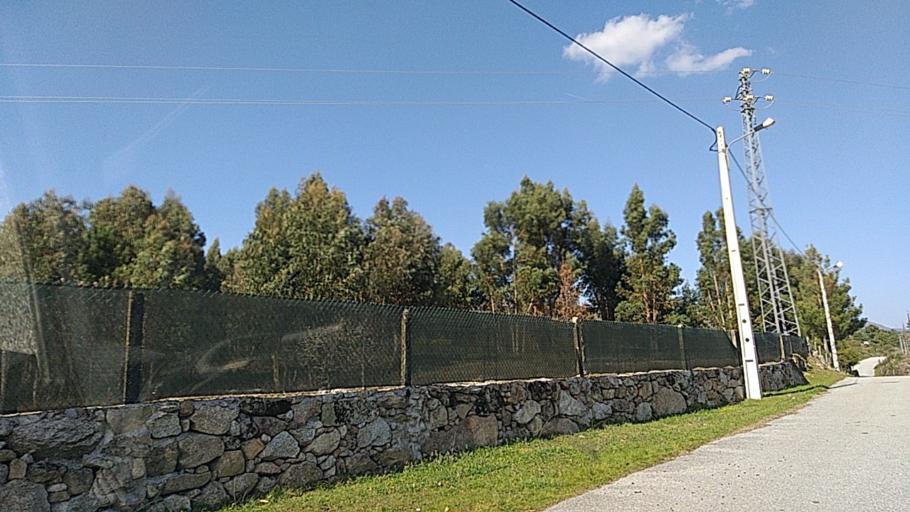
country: PT
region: Guarda
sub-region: Celorico da Beira
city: Celorico da Beira
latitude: 40.6386
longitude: -7.4322
